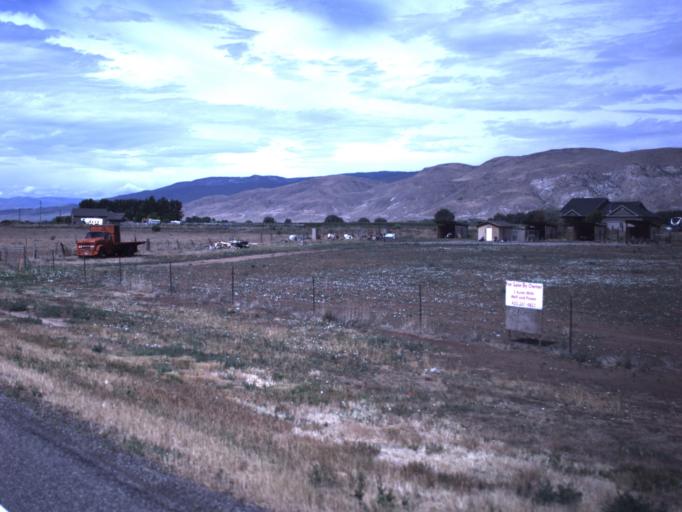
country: US
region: Utah
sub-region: Sevier County
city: Monroe
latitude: 38.6923
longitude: -112.1163
